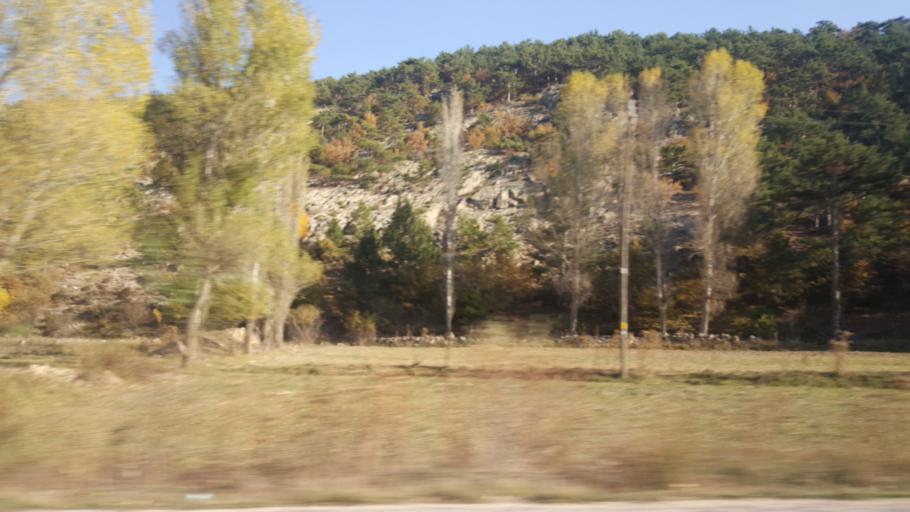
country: TR
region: Eskisehir
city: Kirka
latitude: 39.1380
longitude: 30.5956
